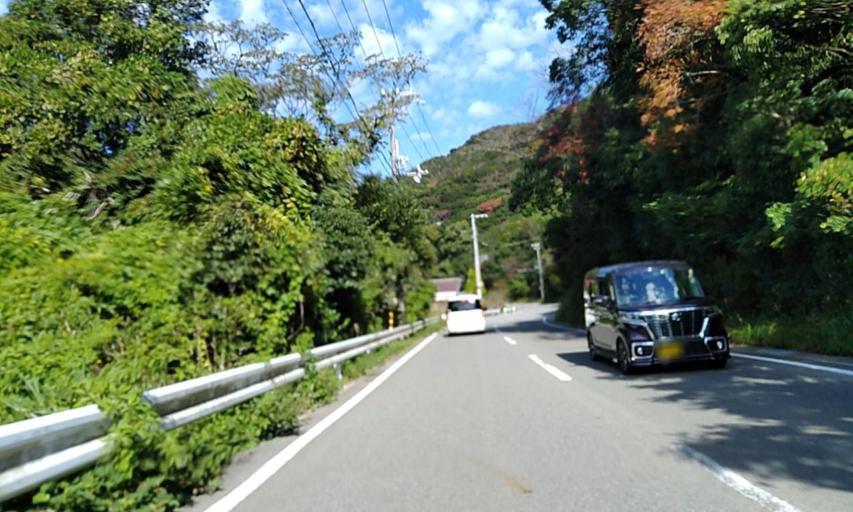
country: JP
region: Wakayama
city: Gobo
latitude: 33.9673
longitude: 135.1178
